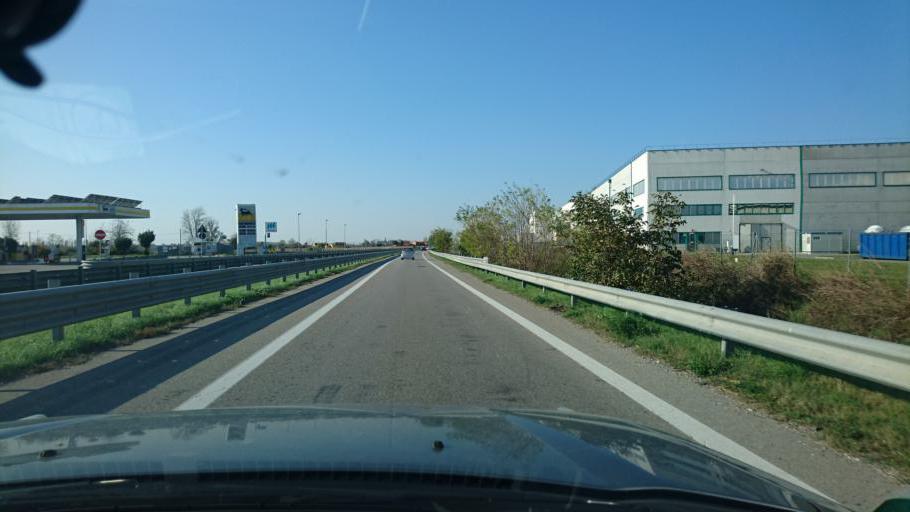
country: IT
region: Veneto
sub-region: Provincia di Padova
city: Monselice
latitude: 45.2079
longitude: 11.7469
